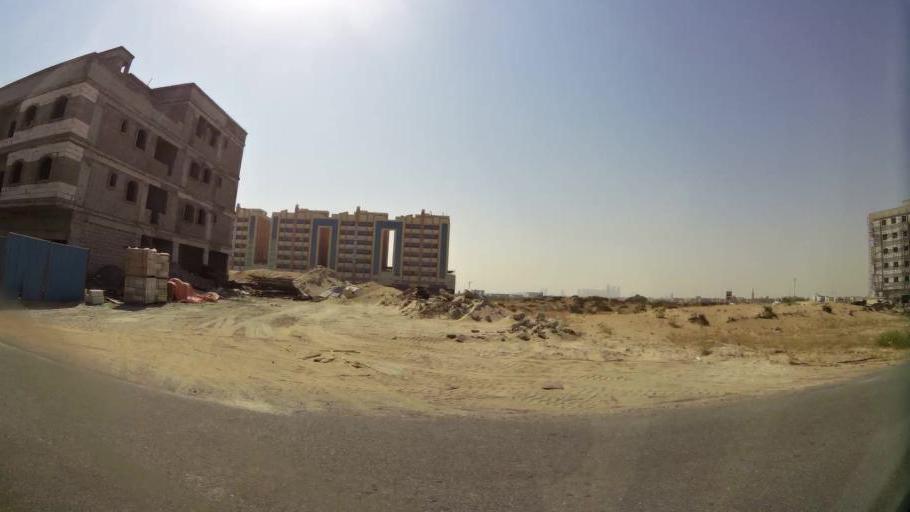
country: AE
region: Ajman
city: Ajman
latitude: 25.4237
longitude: 55.5349
